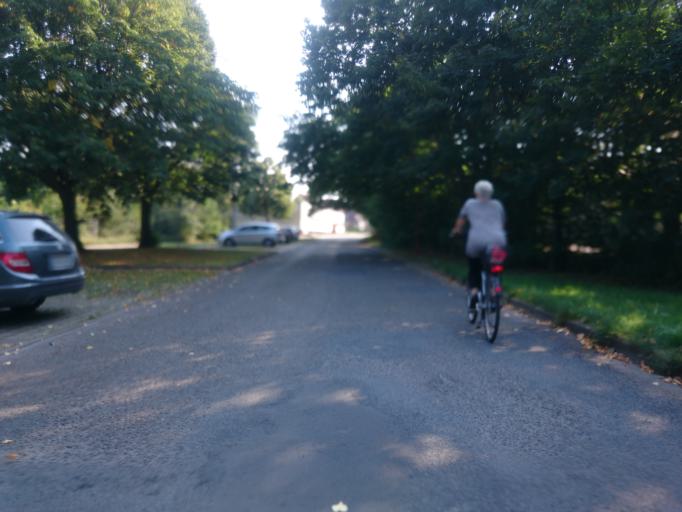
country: DE
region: Mecklenburg-Vorpommern
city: Barth
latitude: 54.3523
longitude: 12.7187
